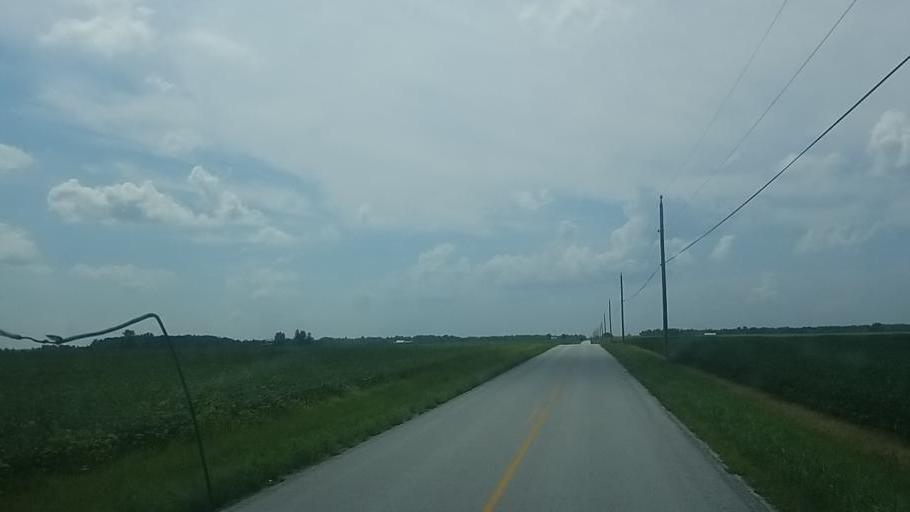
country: US
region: Ohio
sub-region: Hardin County
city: Kenton
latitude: 40.7028
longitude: -83.5822
